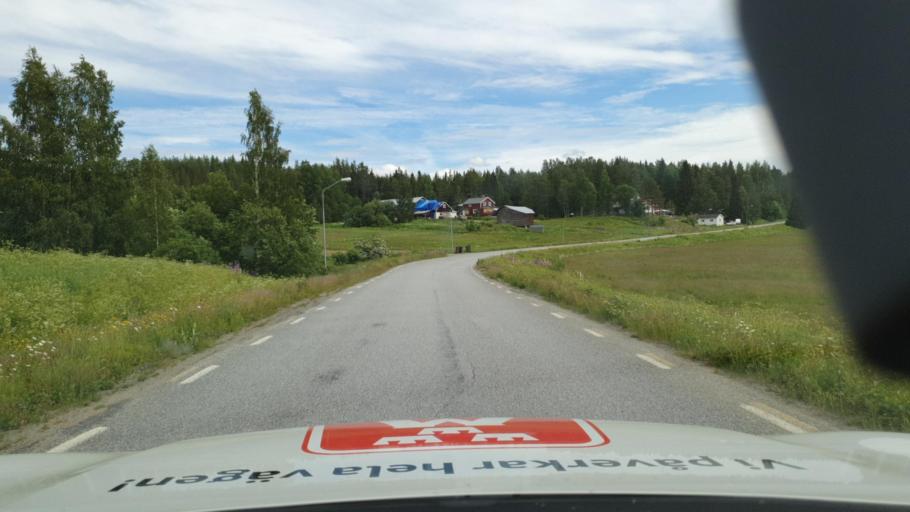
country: SE
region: Vaesterbotten
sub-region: Skelleftea Kommun
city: Burea
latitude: 64.4909
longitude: 21.0305
